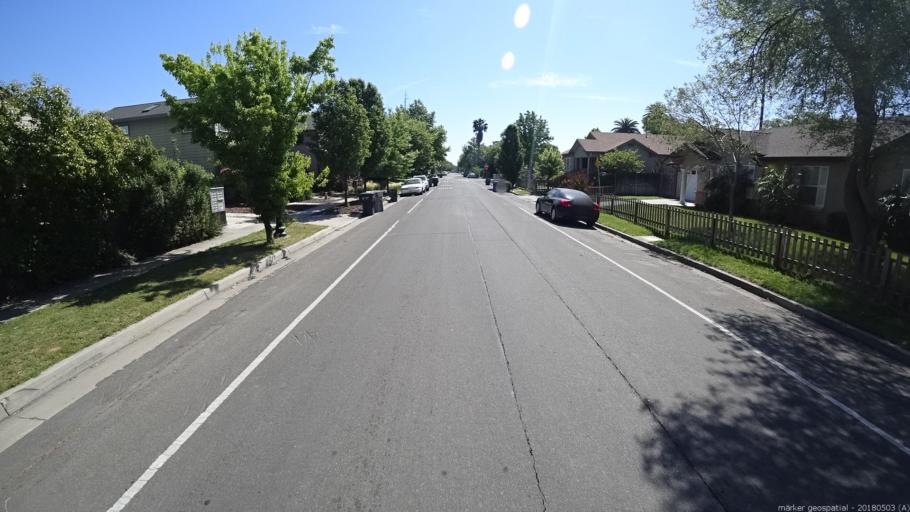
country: US
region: California
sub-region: Sacramento County
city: Sacramento
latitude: 38.6075
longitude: -121.4517
